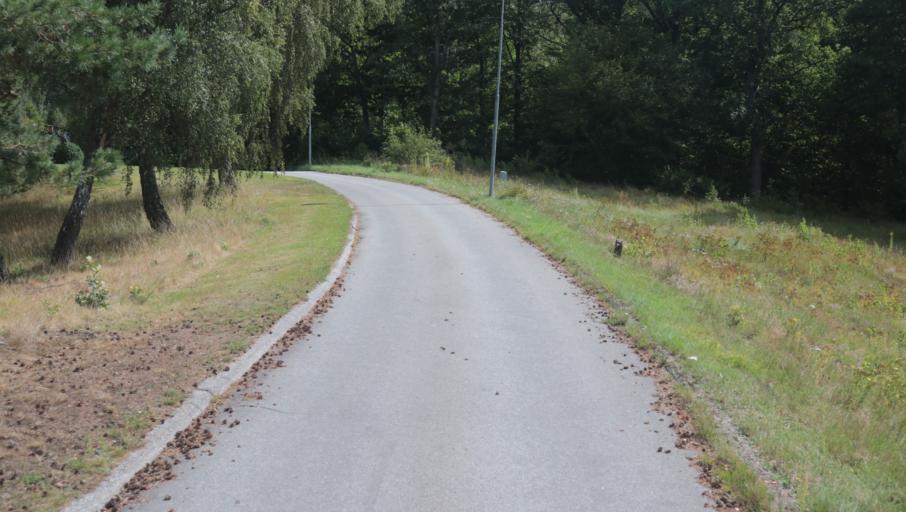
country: SE
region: Blekinge
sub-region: Karlshamns Kommun
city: Svangsta
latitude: 56.2568
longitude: 14.7669
